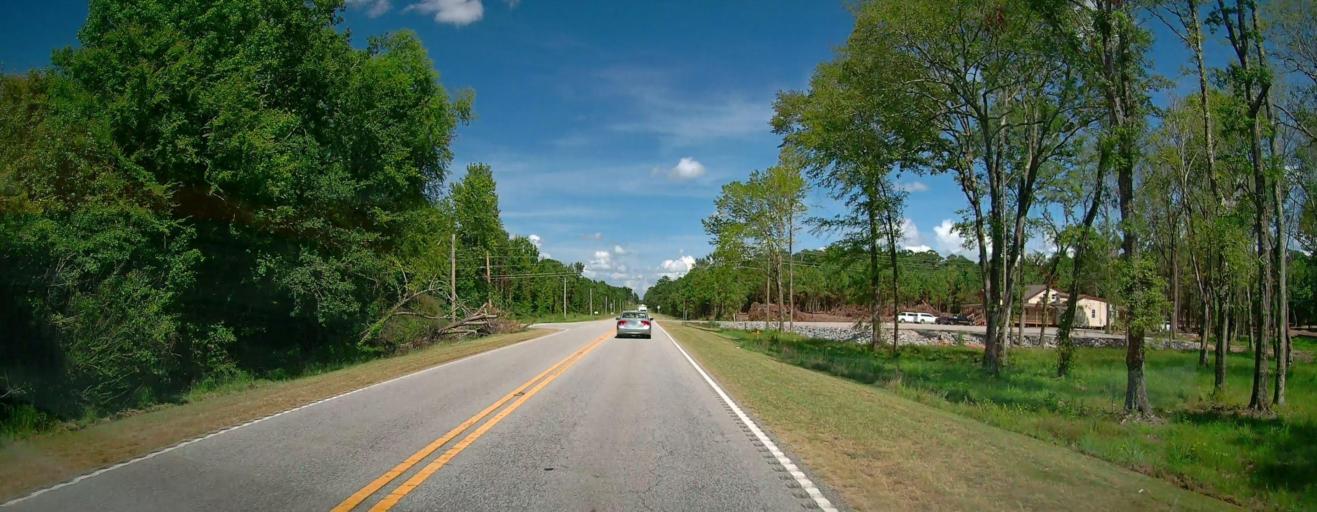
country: US
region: Alabama
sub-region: Elmore County
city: Tallassee
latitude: 32.4000
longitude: -85.9452
